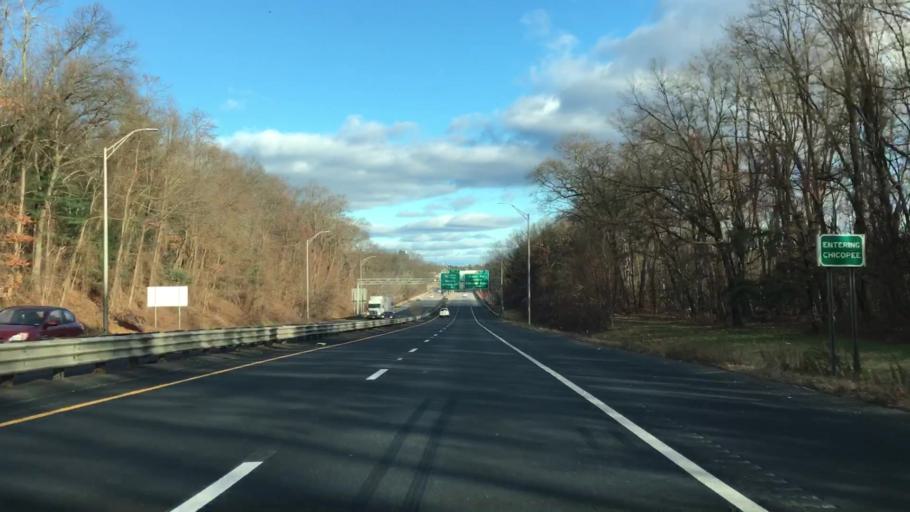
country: US
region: Massachusetts
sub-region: Hampden County
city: North Chicopee
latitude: 42.1541
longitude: -72.5489
